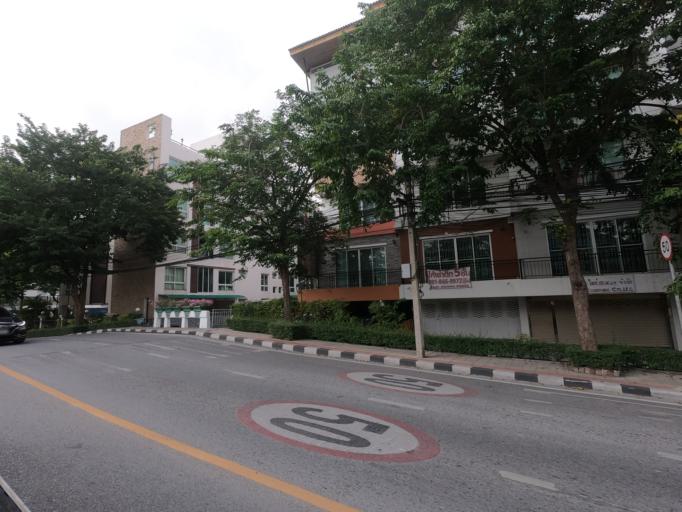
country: TH
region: Bangkok
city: Lat Phrao
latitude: 13.8004
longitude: 100.6067
